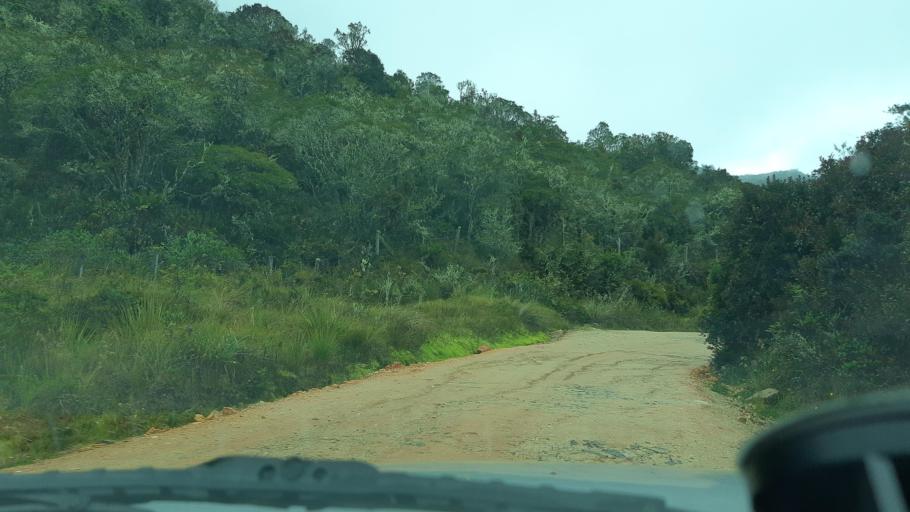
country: CO
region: Cundinamarca
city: Villapinzon
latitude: 5.2112
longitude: -73.5449
